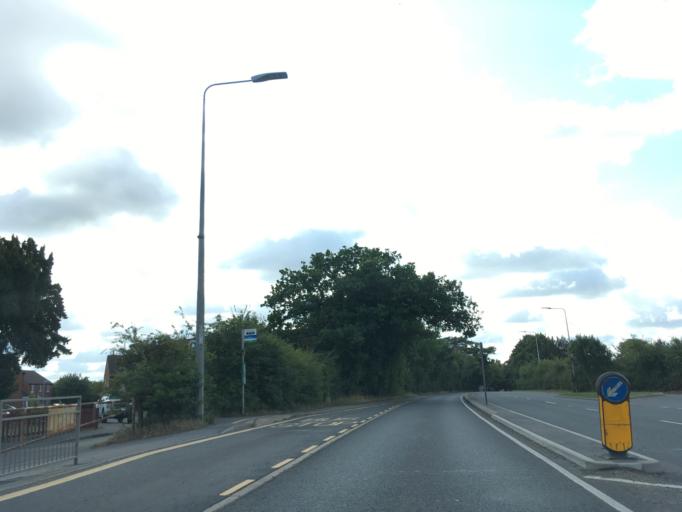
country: GB
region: England
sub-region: West Berkshire
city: Greenham
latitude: 51.3811
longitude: -1.3193
